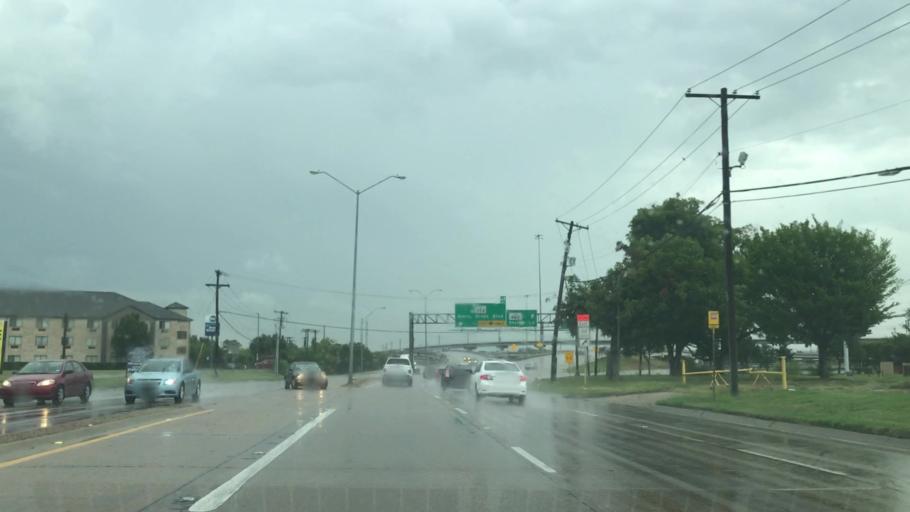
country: US
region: Texas
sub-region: Dallas County
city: Farmers Branch
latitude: 32.8601
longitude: -96.8867
